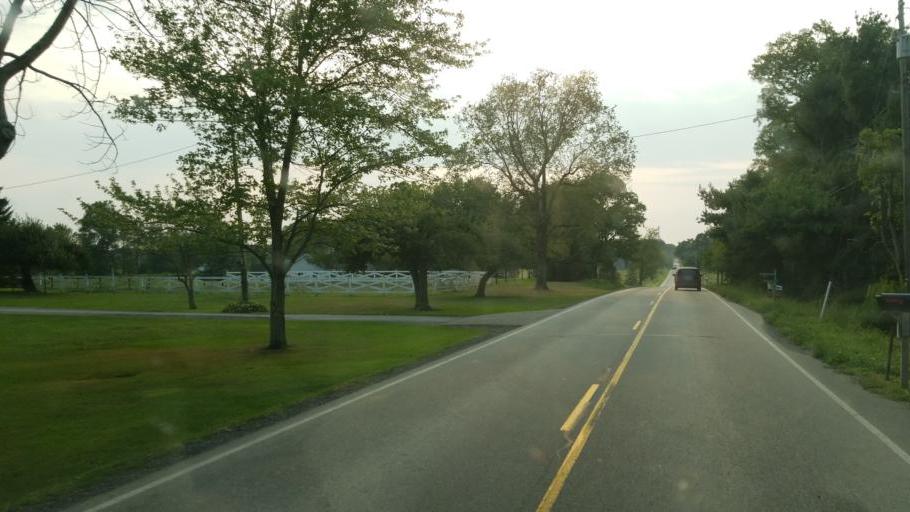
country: US
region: Ohio
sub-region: Portage County
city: Hiram
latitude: 41.3870
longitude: -81.1217
